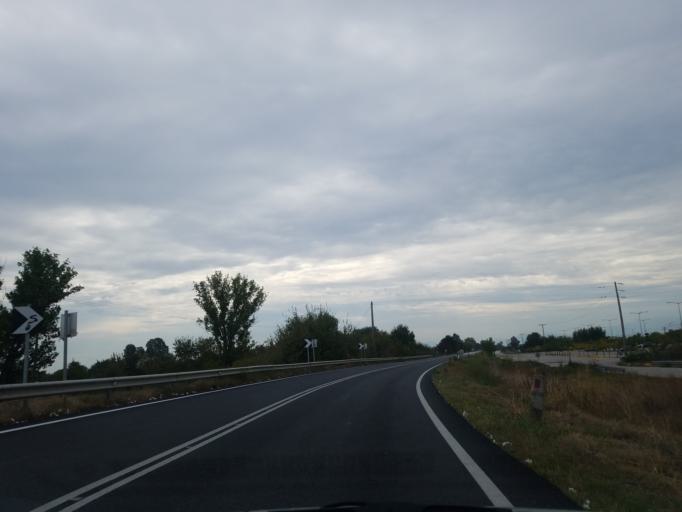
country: GR
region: Thessaly
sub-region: Nomos Kardhitsas
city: Agnantero
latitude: 39.4771
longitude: 21.8454
